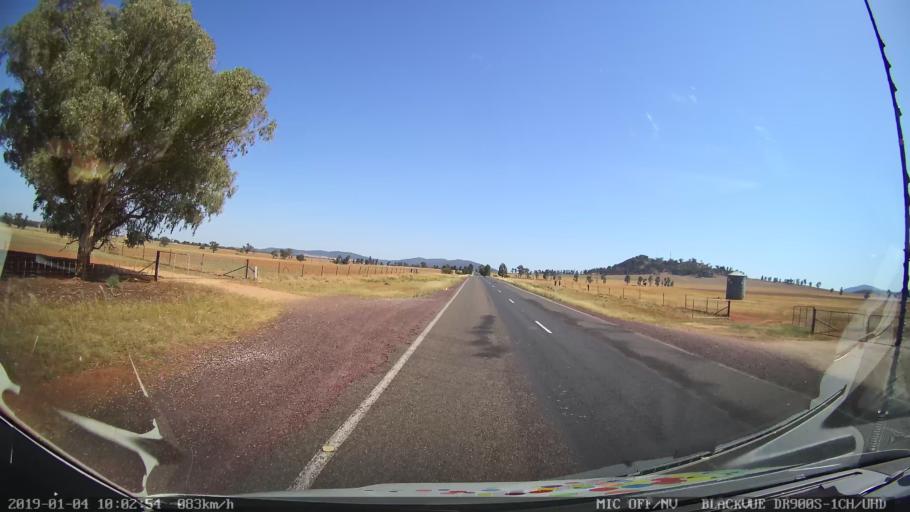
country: AU
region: New South Wales
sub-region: Cabonne
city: Canowindra
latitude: -33.4705
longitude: 148.3650
